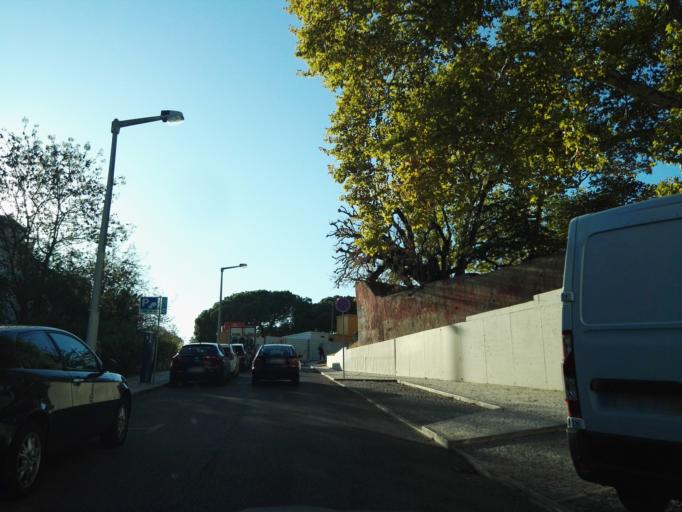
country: PT
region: Lisbon
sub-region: Lisbon
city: Lisbon
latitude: 38.7471
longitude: -9.1347
